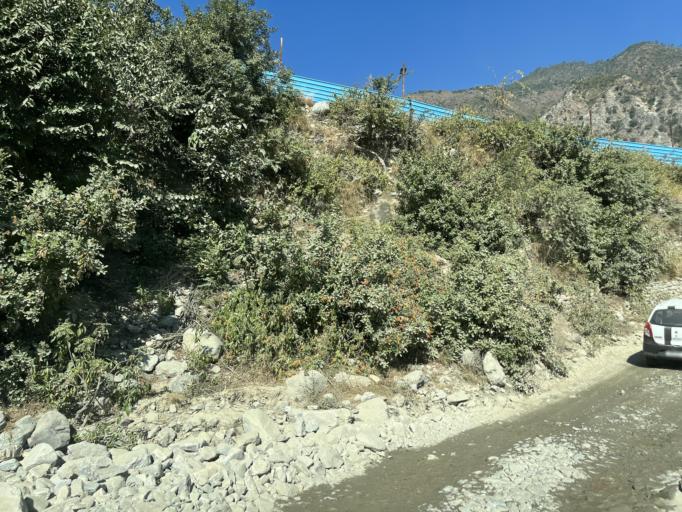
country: IN
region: Uttarakhand
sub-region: Almora
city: Ranikhet
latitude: 29.5504
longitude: 79.4019
